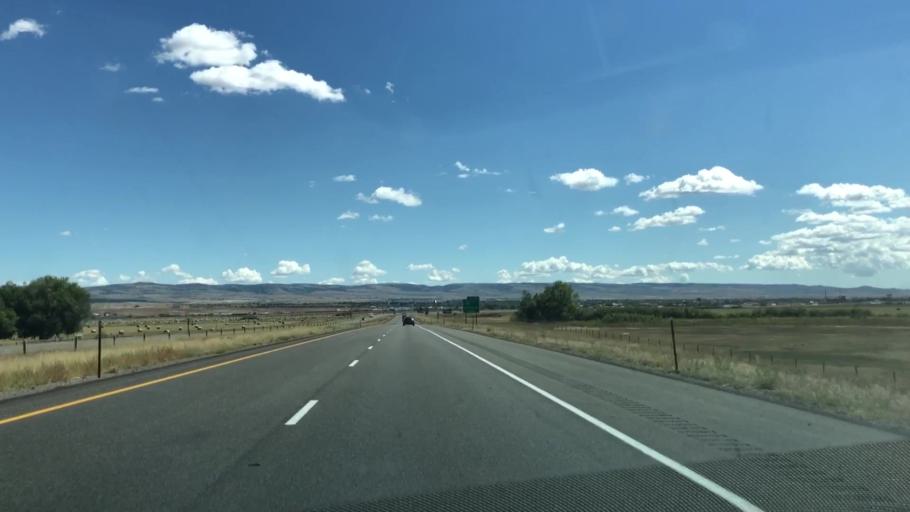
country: US
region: Wyoming
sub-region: Albany County
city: Laramie
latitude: 41.3453
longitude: -105.6279
